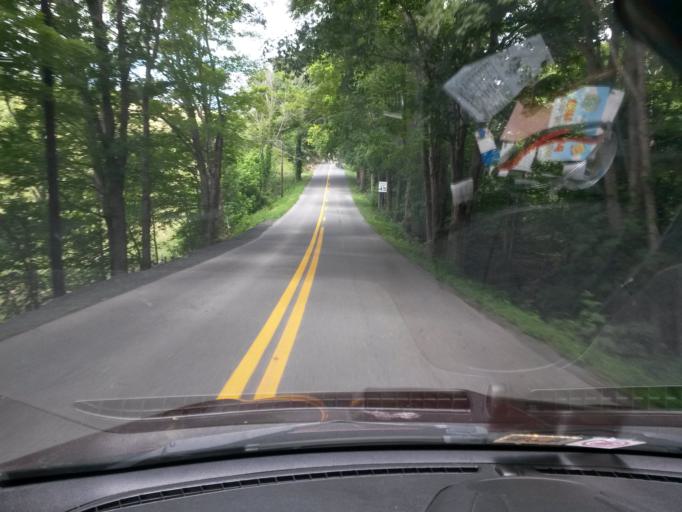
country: US
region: West Virginia
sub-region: Monroe County
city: Union
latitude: 37.5562
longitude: -80.5219
